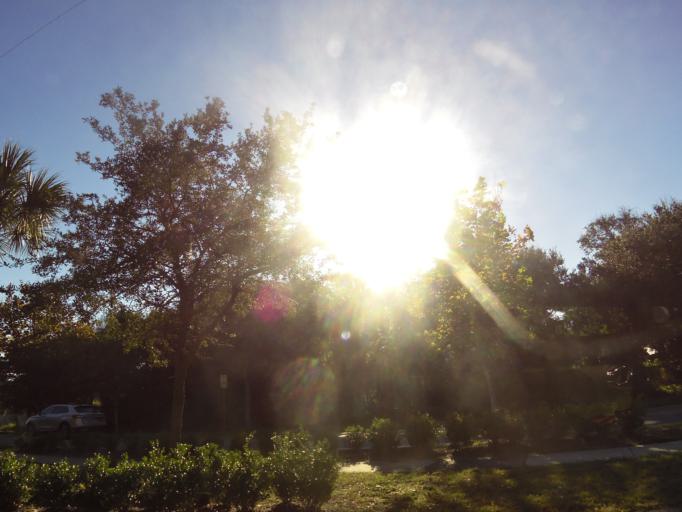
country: US
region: Florida
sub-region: Duval County
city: Atlantic Beach
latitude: 30.3416
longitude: -81.3989
